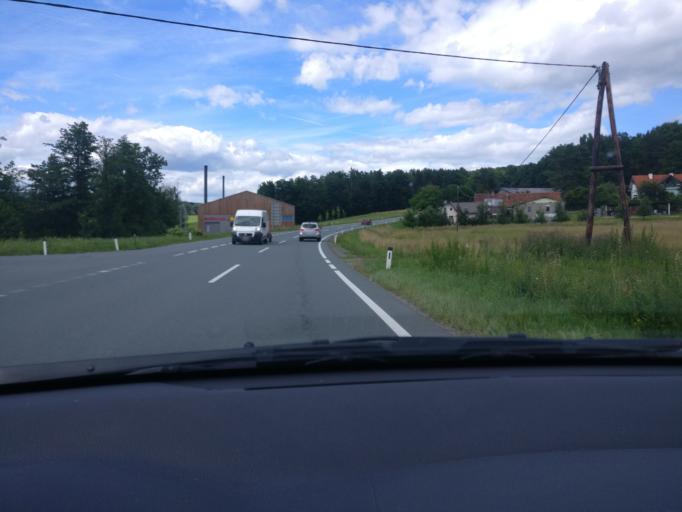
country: AT
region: Styria
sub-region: Politischer Bezirk Weiz
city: Hirnsdorf
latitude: 47.1799
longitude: 15.8105
